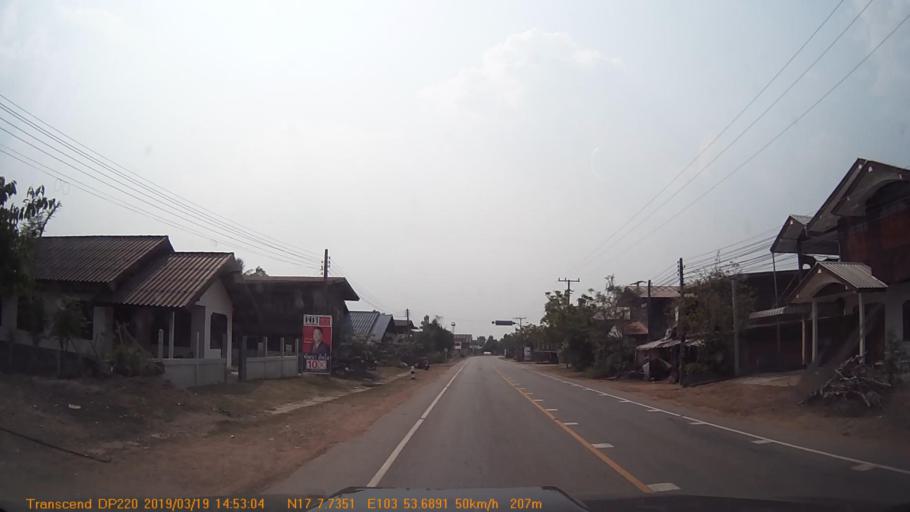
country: TH
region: Sakon Nakhon
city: Kut Bak
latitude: 17.1290
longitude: 103.8947
